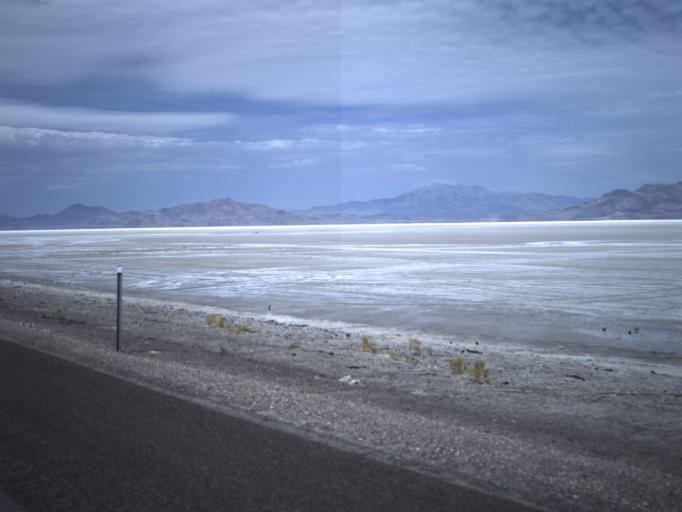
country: US
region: Utah
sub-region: Tooele County
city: Wendover
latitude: 40.7363
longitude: -113.7011
